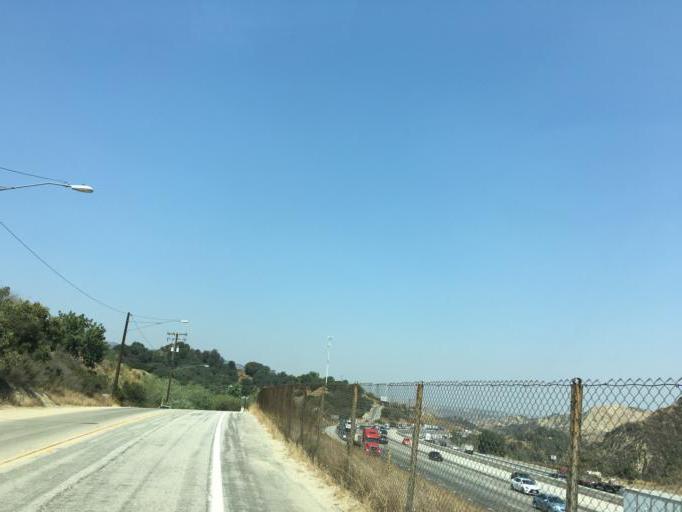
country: US
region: California
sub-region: Los Angeles County
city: Santa Clarita
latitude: 34.3411
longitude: -118.5261
